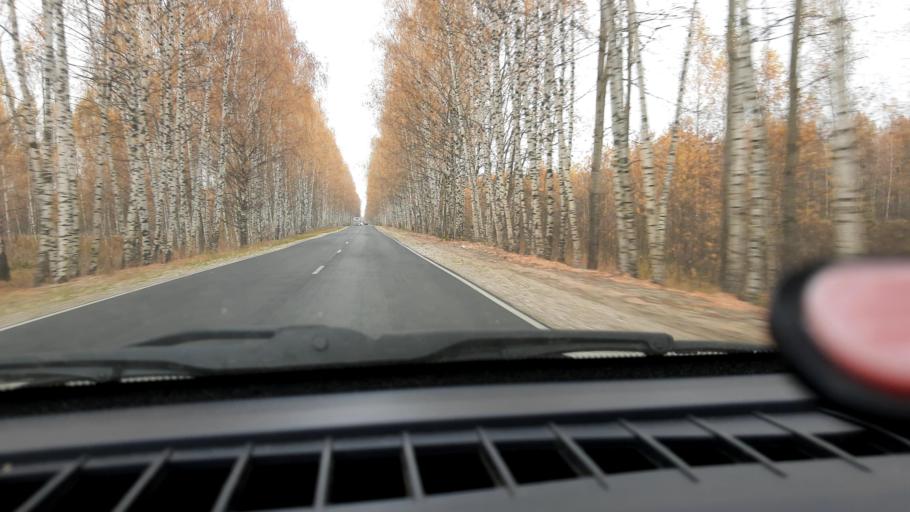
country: RU
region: Nizjnij Novgorod
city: Neklyudovo
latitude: 56.4850
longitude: 43.8663
